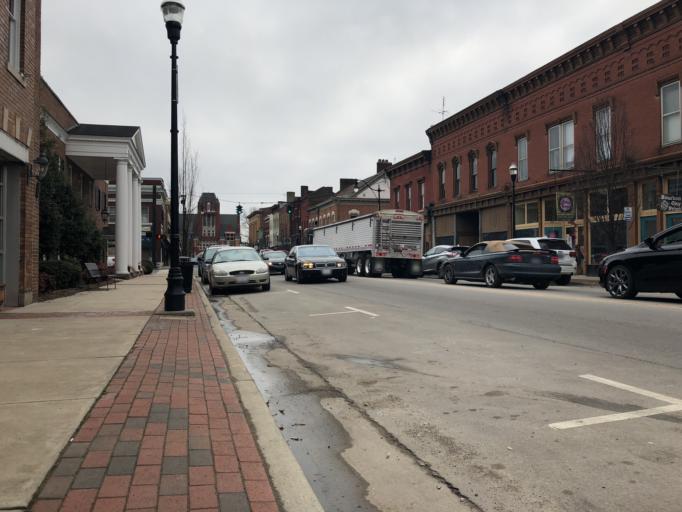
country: US
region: Kentucky
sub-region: Nelson County
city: Bardstown
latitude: 37.8110
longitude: -85.4662
